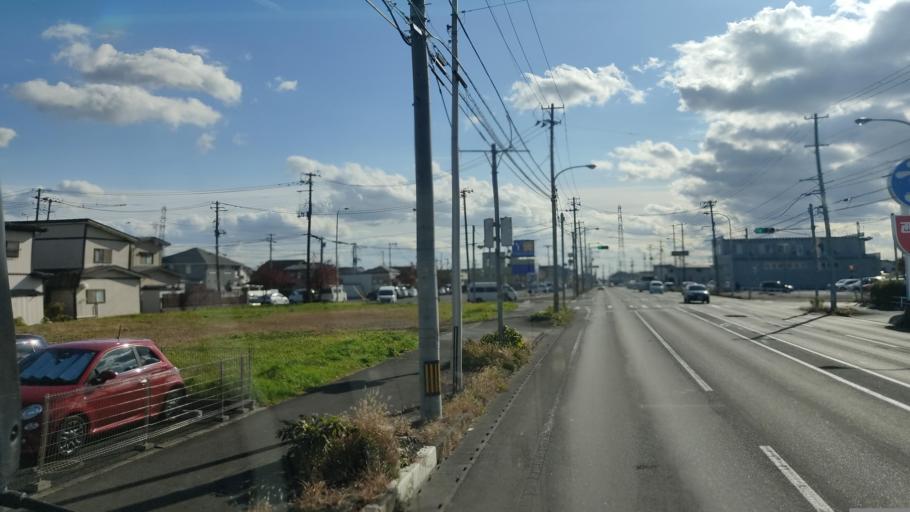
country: JP
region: Iwate
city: Morioka-shi
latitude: 39.6830
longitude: 141.1434
